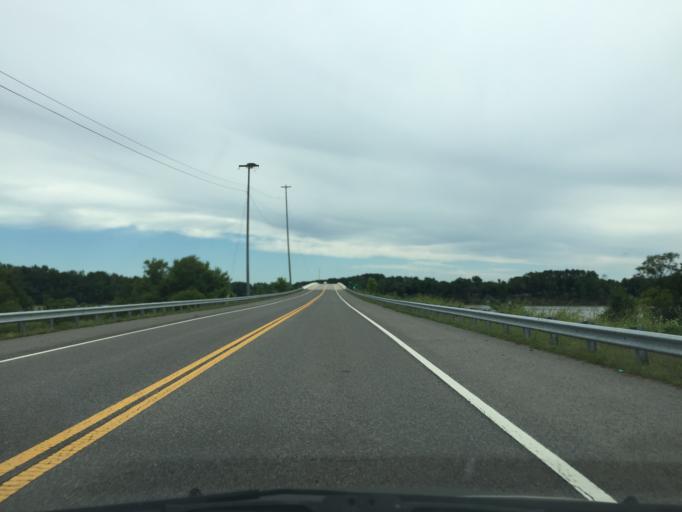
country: US
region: Tennessee
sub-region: Bradley County
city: Hopewell
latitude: 35.3632
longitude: -84.9120
